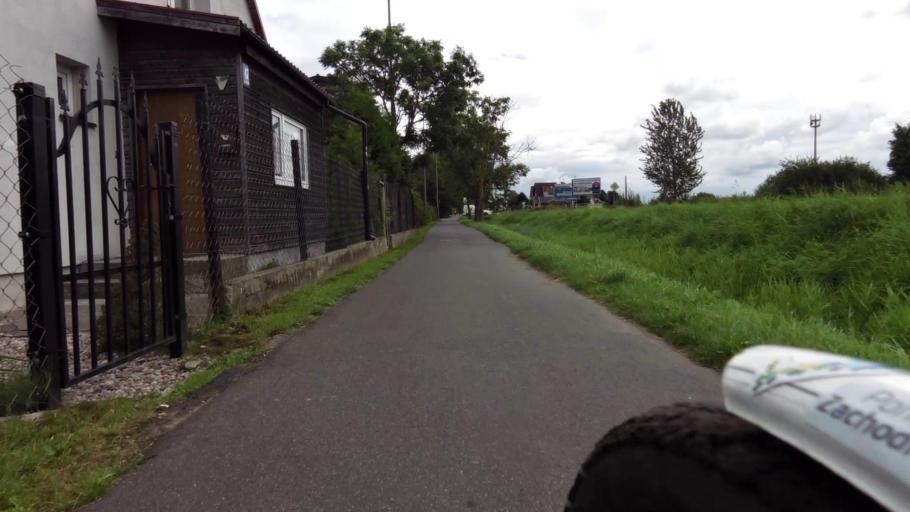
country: PL
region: West Pomeranian Voivodeship
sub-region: Powiat koszalinski
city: Mielno
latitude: 54.2528
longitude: 16.0568
